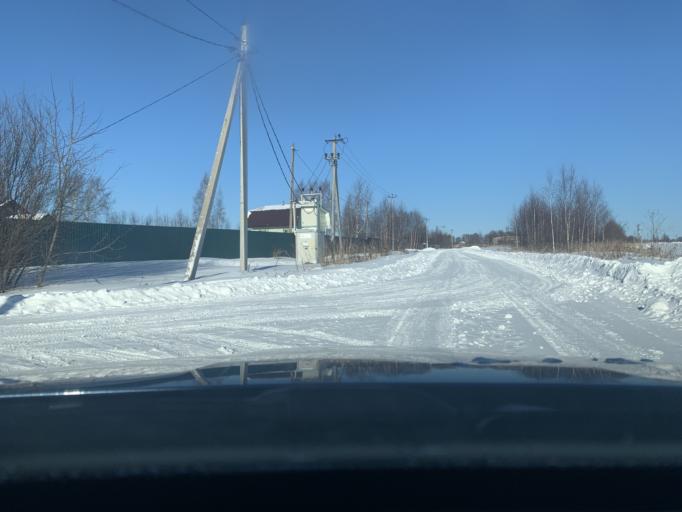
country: RU
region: Jaroslavl
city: Tunoshna
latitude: 57.6510
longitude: 40.0679
